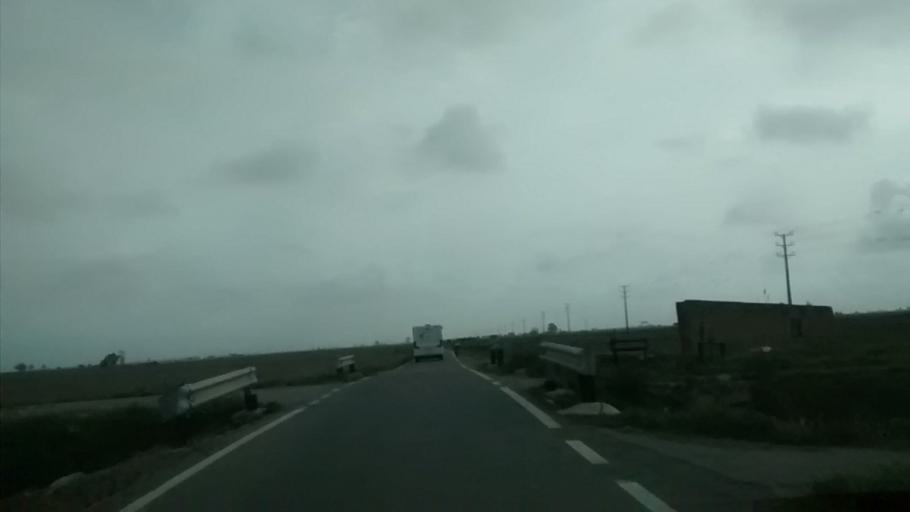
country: ES
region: Catalonia
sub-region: Provincia de Tarragona
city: Sant Carles de la Rapita
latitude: 40.6580
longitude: 0.6344
